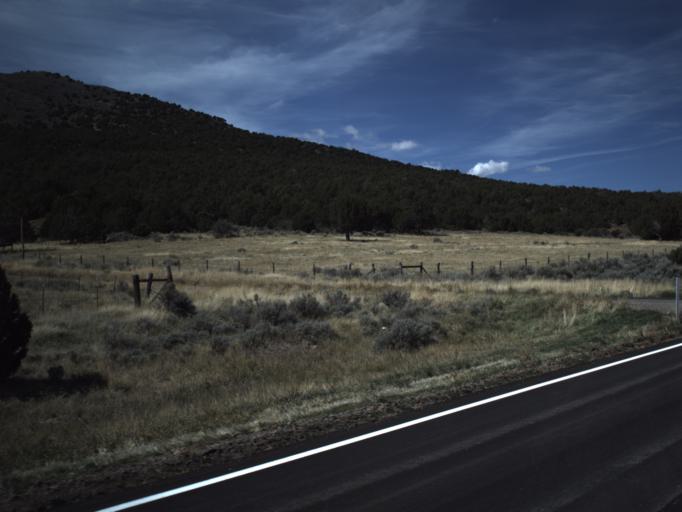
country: US
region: Utah
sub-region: Washington County
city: Enterprise
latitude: 37.5065
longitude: -113.6327
